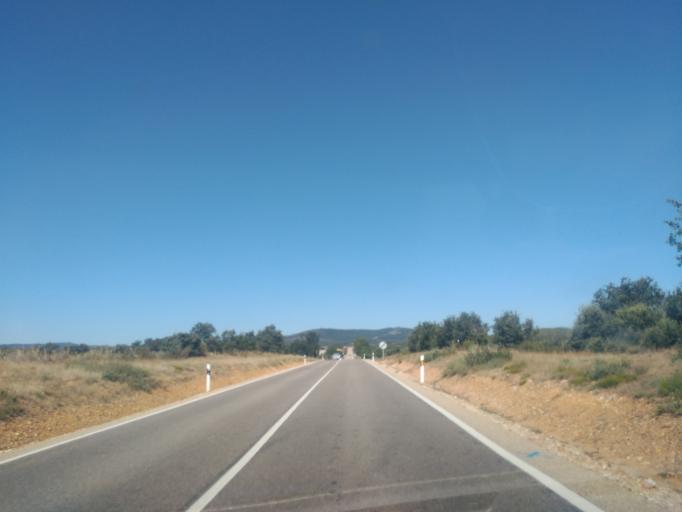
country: ES
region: Castille and Leon
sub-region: Provincia de Zamora
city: Ferreras de Abajo
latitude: 41.8999
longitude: -6.0485
